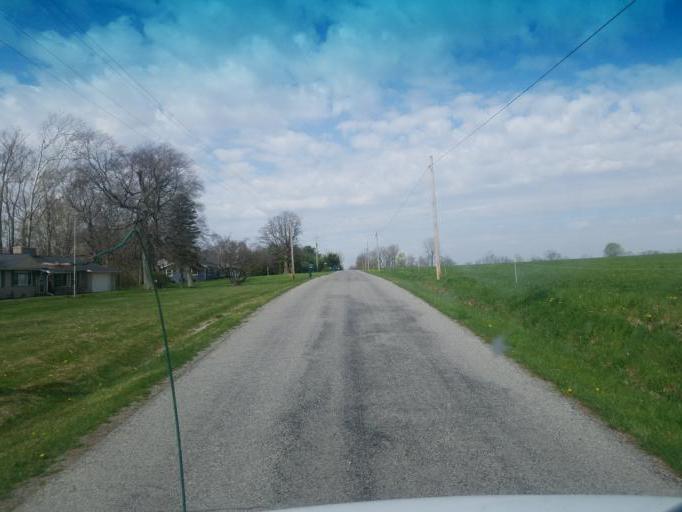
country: US
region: Ohio
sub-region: Logan County
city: Northwood
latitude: 40.4912
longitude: -83.7304
